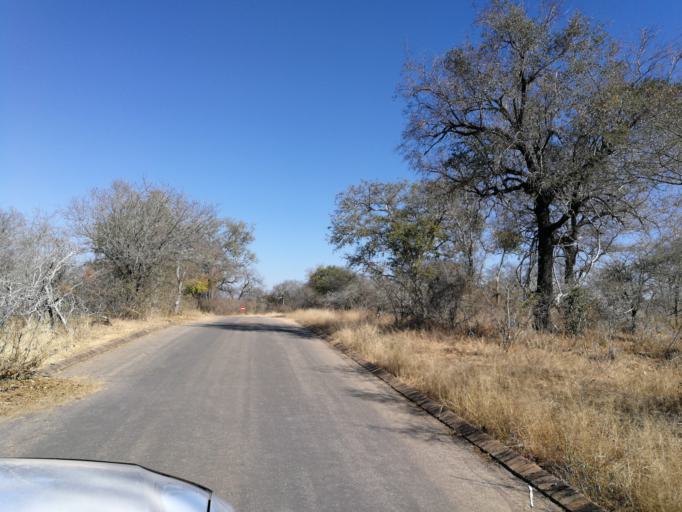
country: ZA
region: Limpopo
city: Thulamahashi
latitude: -24.9835
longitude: 31.5772
